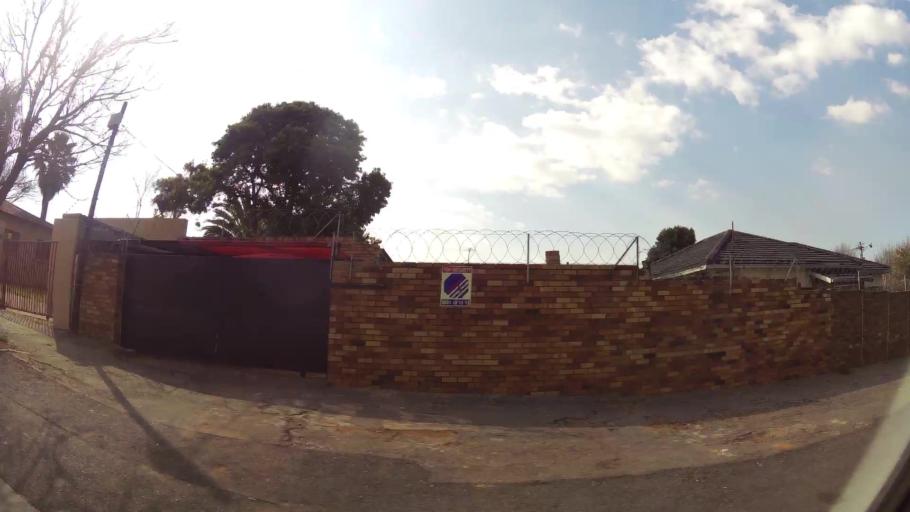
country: ZA
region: Gauteng
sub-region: Ekurhuleni Metropolitan Municipality
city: Germiston
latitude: -26.1782
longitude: 28.1809
